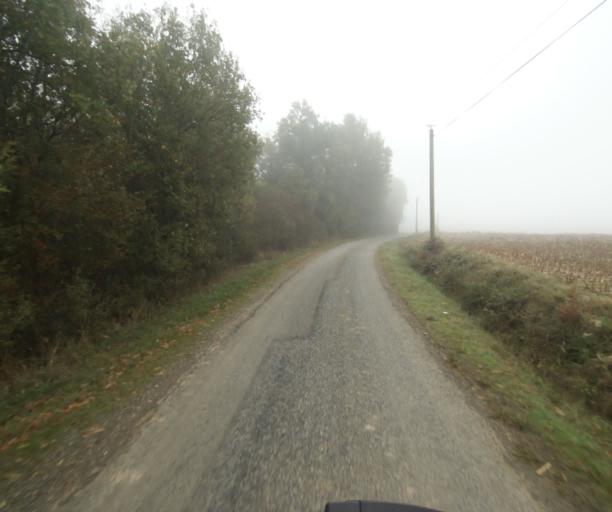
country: FR
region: Midi-Pyrenees
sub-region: Departement du Tarn-et-Garonne
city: Nohic
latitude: 43.9087
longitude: 1.4731
